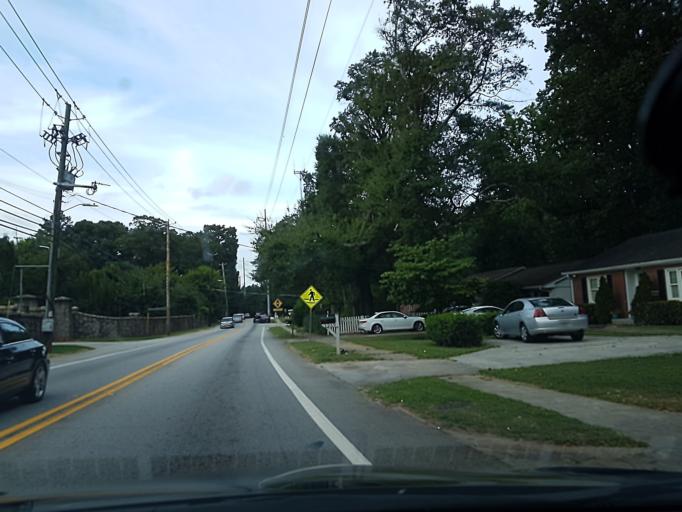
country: US
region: Georgia
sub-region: DeKalb County
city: Druid Hills
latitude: 33.7887
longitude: -84.3393
